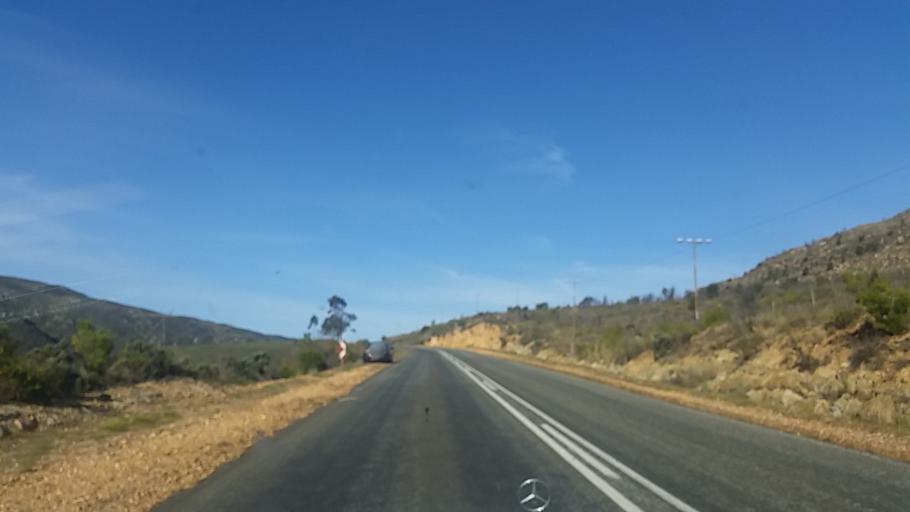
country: ZA
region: Western Cape
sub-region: Eden District Municipality
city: Knysna
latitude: -33.7530
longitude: 22.9479
